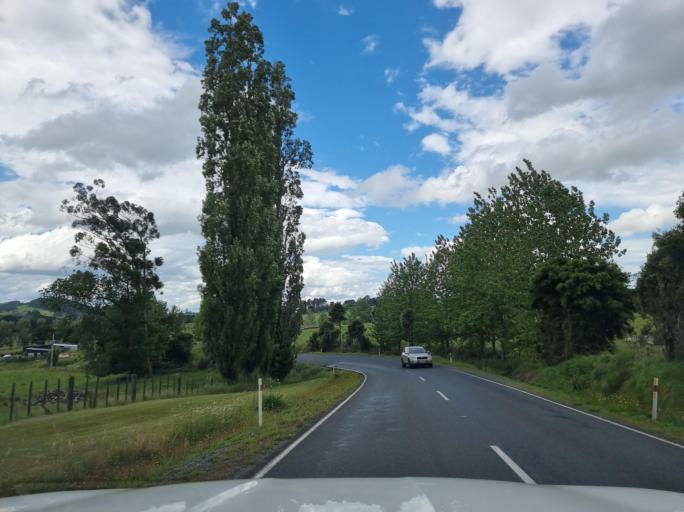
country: NZ
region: Northland
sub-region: Whangarei
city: Maungatapere
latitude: -35.8570
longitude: 174.2535
